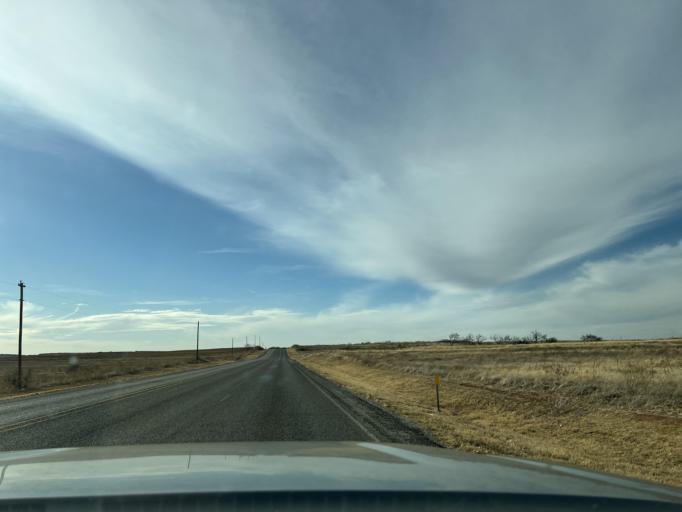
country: US
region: Texas
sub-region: Fisher County
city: Rotan
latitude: 32.7393
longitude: -100.5312
